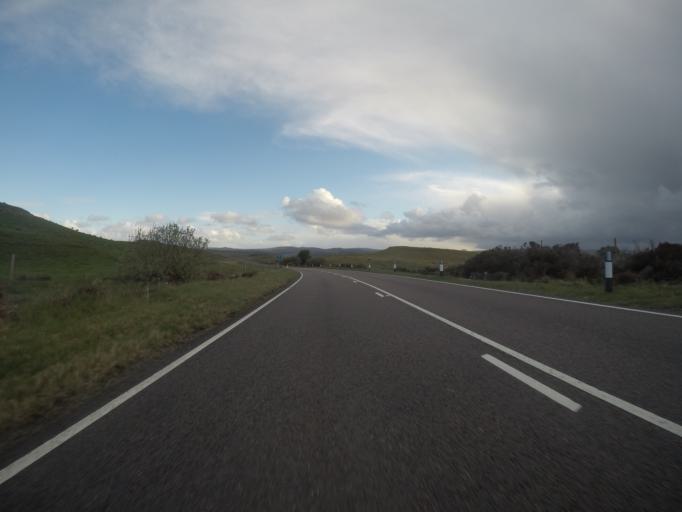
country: GB
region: Scotland
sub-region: Highland
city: Portree
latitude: 57.5461
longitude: -6.3652
